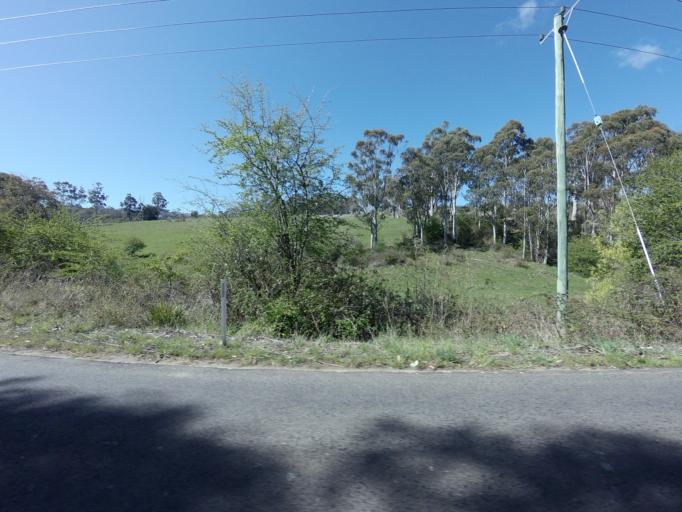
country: AU
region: Tasmania
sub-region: Derwent Valley
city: New Norfolk
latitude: -42.6250
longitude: 146.7226
